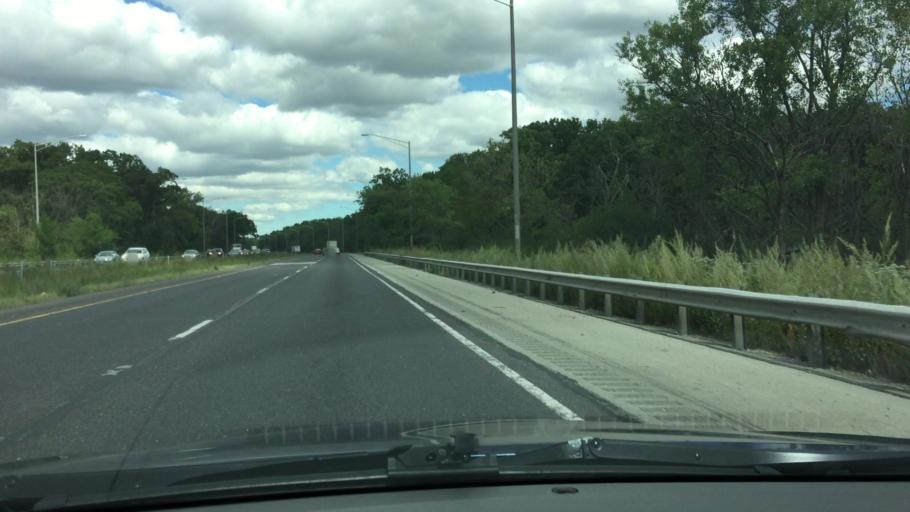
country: US
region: Illinois
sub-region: Cook County
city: Glenwood
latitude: 41.5446
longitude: -87.5824
